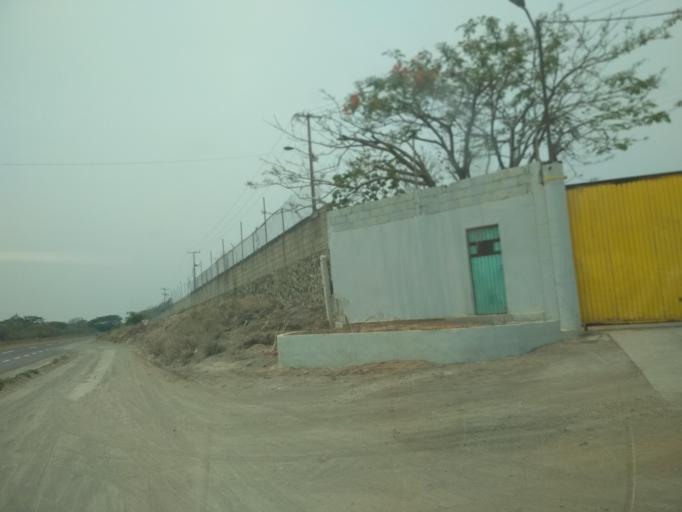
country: MX
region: Veracruz
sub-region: Veracruz
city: Delfino Victoria (Santa Fe)
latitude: 19.2168
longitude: -96.2582
